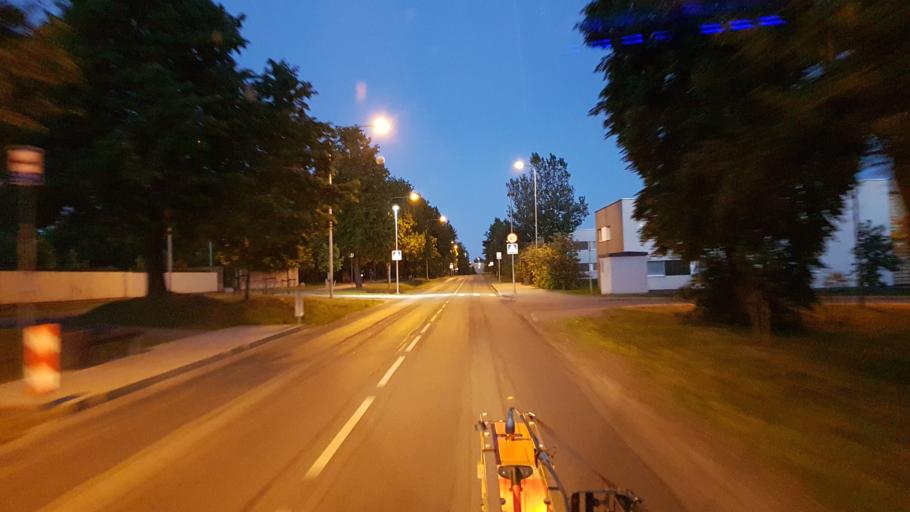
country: EE
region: Harju
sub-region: Saue vald
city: Laagri
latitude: 59.4320
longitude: 24.6214
